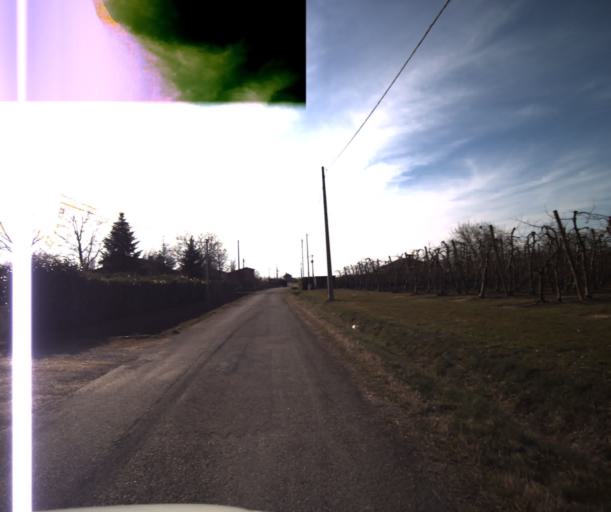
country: FR
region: Midi-Pyrenees
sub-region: Departement du Tarn-et-Garonne
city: Corbarieu
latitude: 43.9380
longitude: 1.3546
